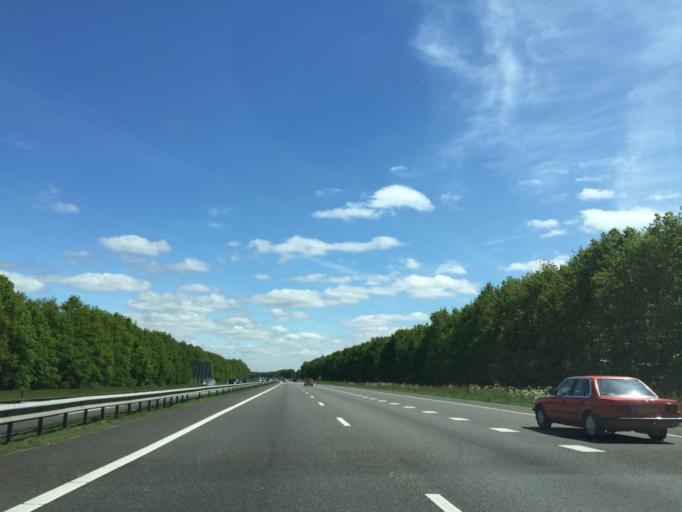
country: NL
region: Gelderland
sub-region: Gemeente Barneveld
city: Voorthuizen
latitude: 52.1687
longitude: 5.5978
